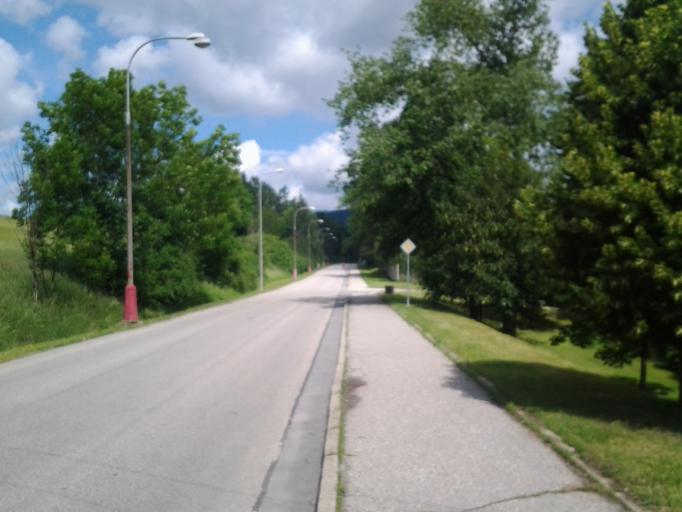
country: CZ
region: Jihocesky
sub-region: Okres Cesky Krumlov
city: Cesky Krumlov
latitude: 48.8238
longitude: 14.3094
